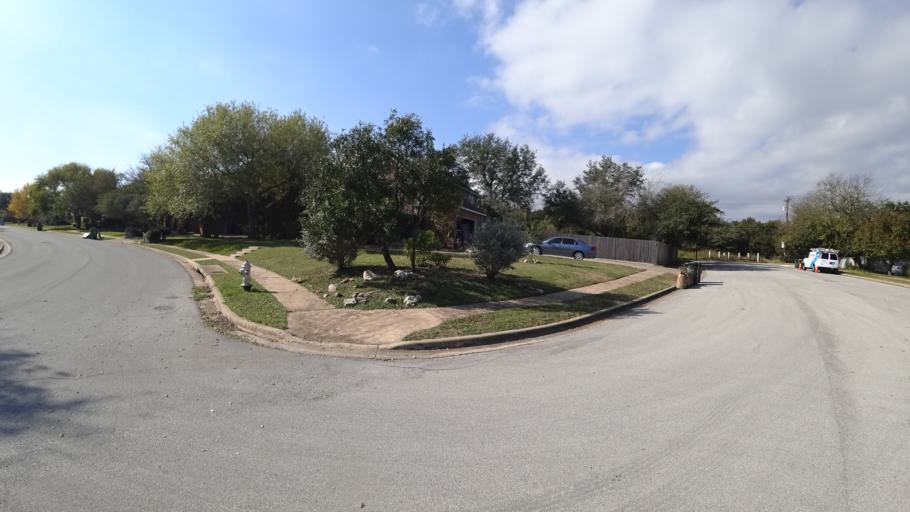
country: US
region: Texas
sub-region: Travis County
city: Shady Hollow
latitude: 30.1681
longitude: -97.8701
